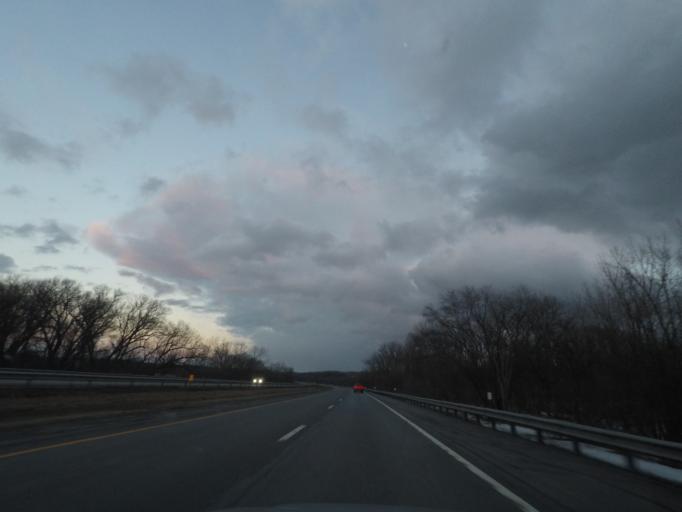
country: US
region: New York
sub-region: Montgomery County
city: Tribes Hill
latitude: 42.9307
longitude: -74.3116
